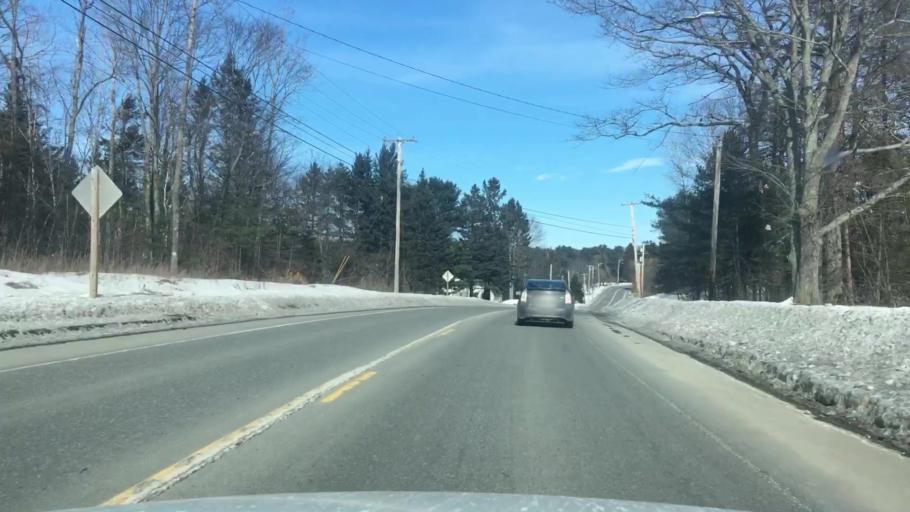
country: US
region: Maine
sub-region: Penobscot County
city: Orrington
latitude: 44.7383
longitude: -68.8196
